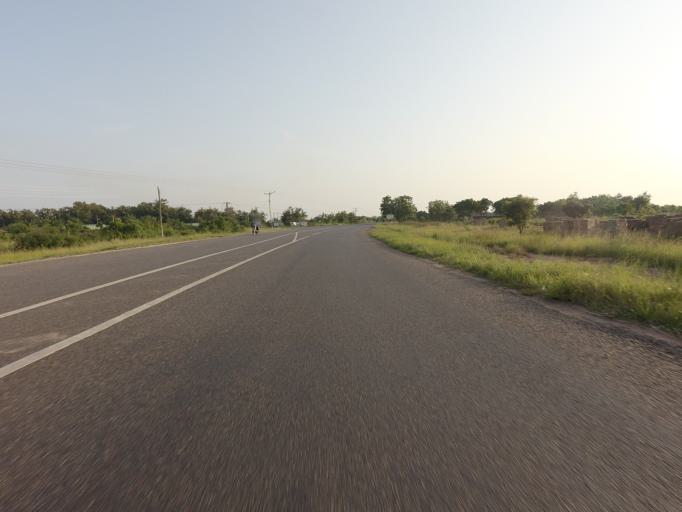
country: GH
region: Volta
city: Anloga
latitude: 5.9724
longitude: 0.6655
